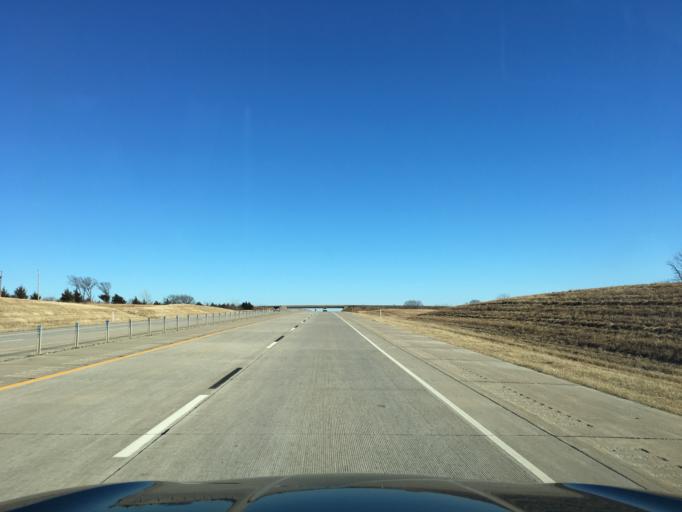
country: US
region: Oklahoma
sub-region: Payne County
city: Yale
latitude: 36.2249
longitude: -96.7012
